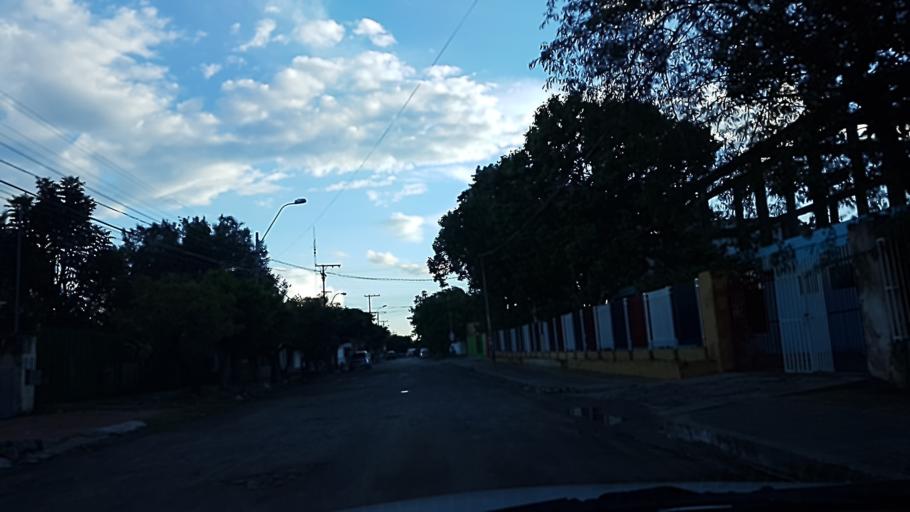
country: PY
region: Central
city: Colonia Mariano Roque Alonso
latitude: -25.2119
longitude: -57.5325
